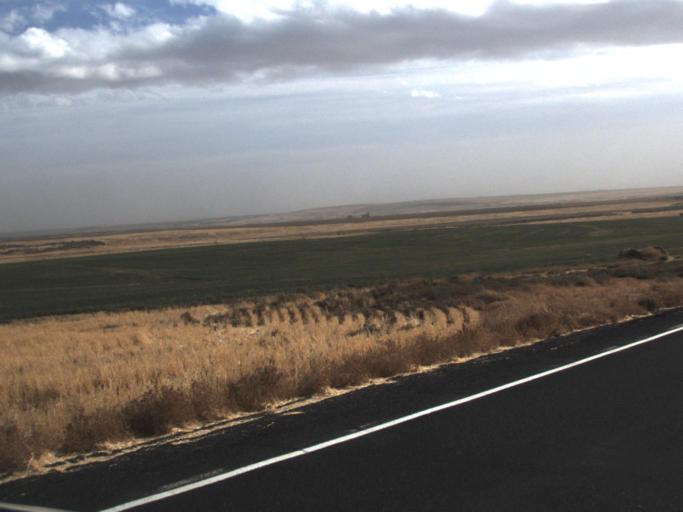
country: US
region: Washington
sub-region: Okanogan County
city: Coulee Dam
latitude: 47.5795
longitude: -118.7859
